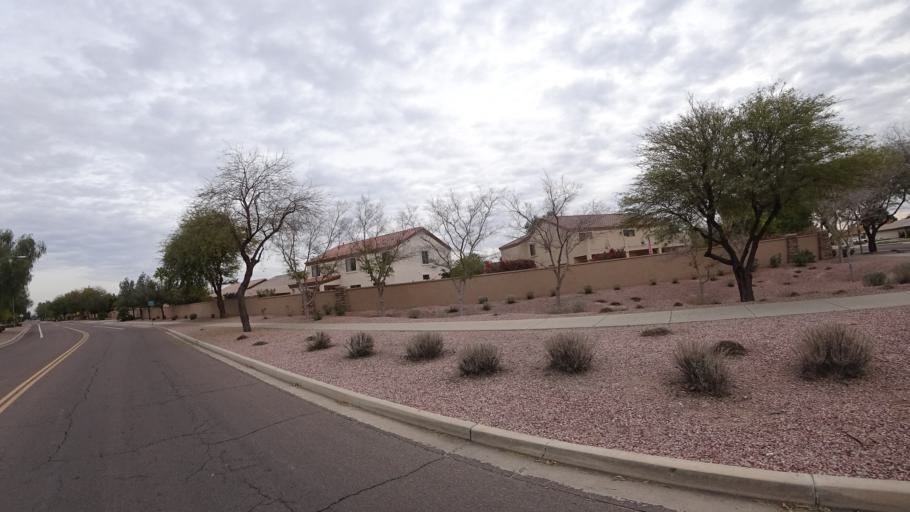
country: US
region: Arizona
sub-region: Maricopa County
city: Peoria
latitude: 33.6472
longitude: -112.1775
